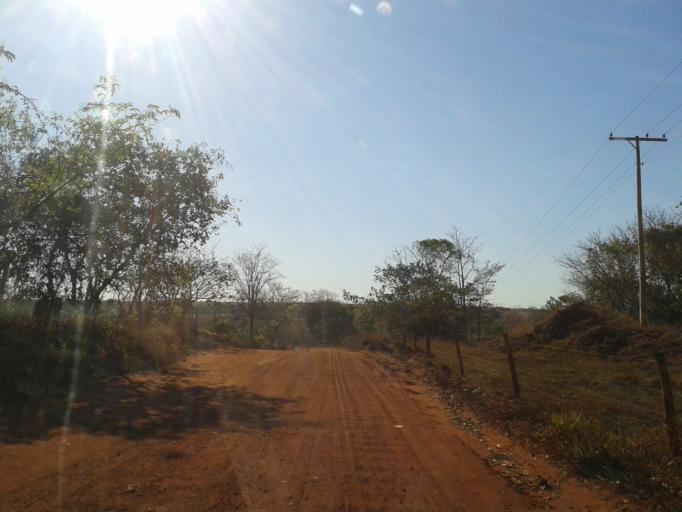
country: BR
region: Minas Gerais
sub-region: Ituiutaba
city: Ituiutaba
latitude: -18.9773
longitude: -49.4258
